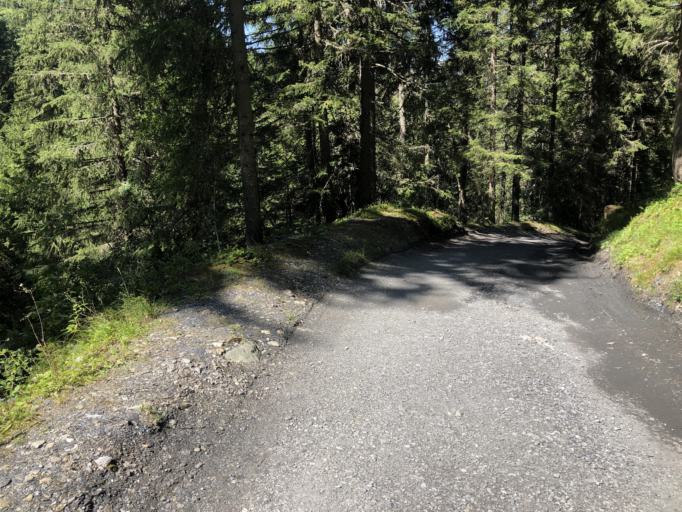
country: FR
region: Rhone-Alpes
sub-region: Departement de la Haute-Savoie
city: Saint-Gervais-les-Bains
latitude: 45.8609
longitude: 6.6825
